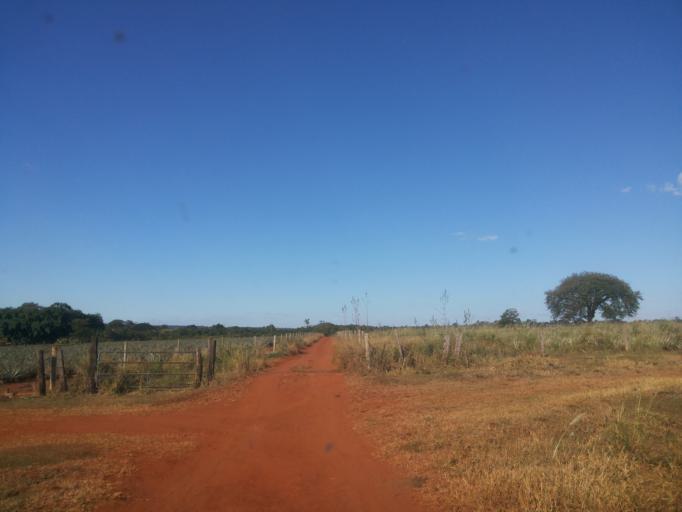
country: BR
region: Minas Gerais
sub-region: Centralina
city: Centralina
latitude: -18.7392
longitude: -49.1656
